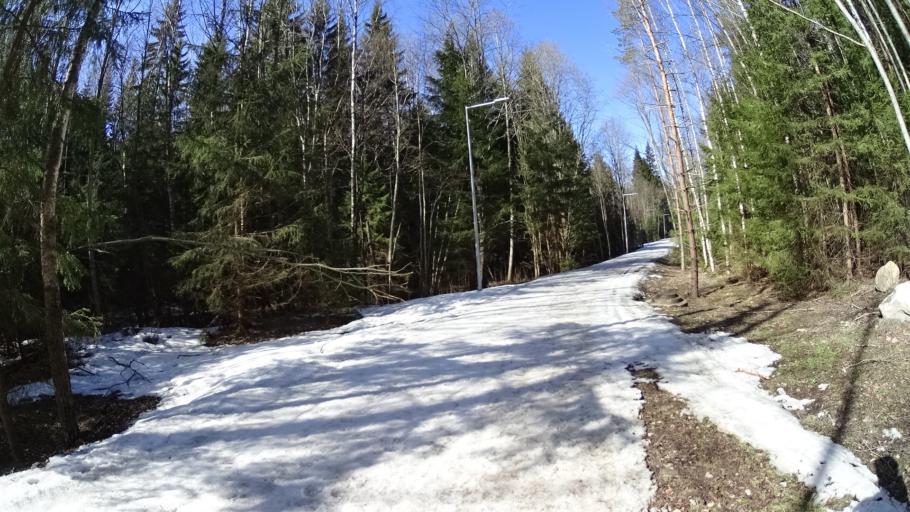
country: FI
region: Uusimaa
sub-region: Helsinki
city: Espoo
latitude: 60.1837
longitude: 24.6841
